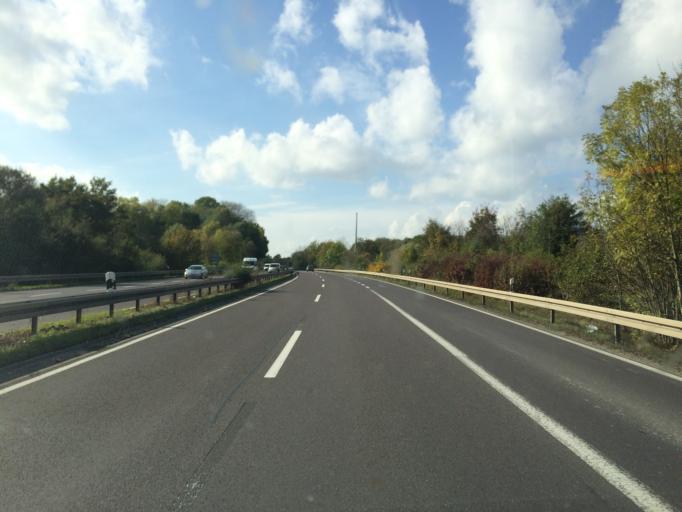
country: DE
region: Lower Saxony
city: Laatzen
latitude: 52.3601
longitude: 9.8726
